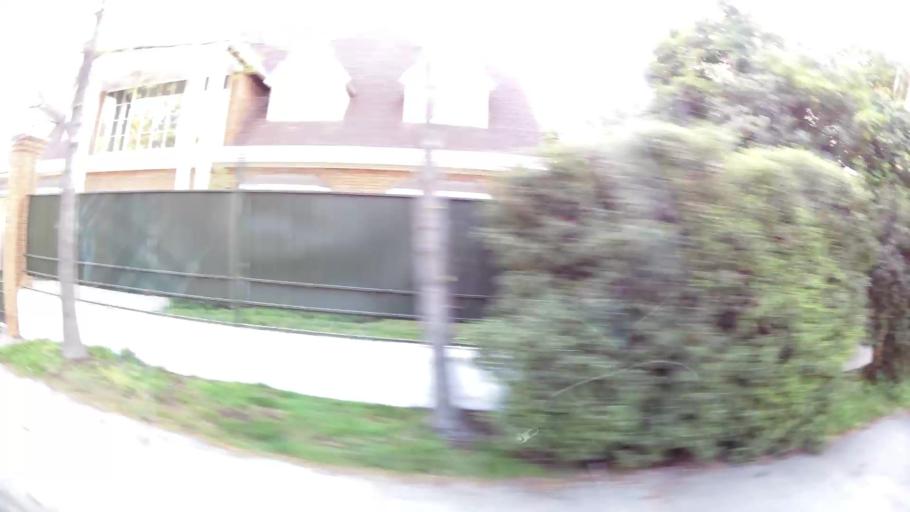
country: CL
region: Santiago Metropolitan
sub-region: Provincia de Santiago
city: Villa Presidente Frei, Nunoa, Santiago, Chile
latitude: -33.3515
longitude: -70.5393
